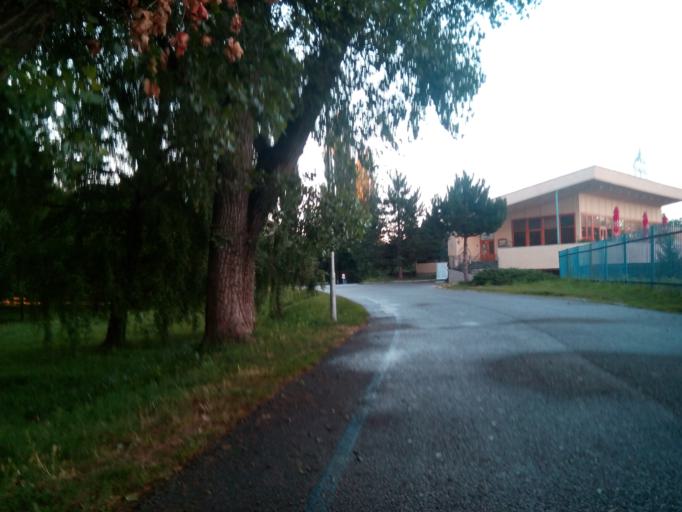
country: SK
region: Kosicky
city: Kosice
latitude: 48.7445
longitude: 21.2547
